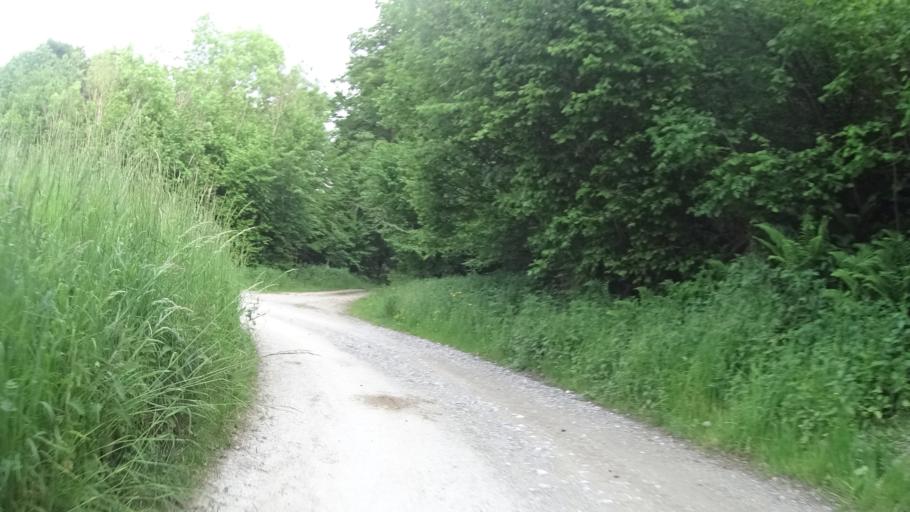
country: CH
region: Aargau
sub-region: Bezirk Zurzach
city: Leibstadt
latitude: 47.6034
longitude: 8.1856
